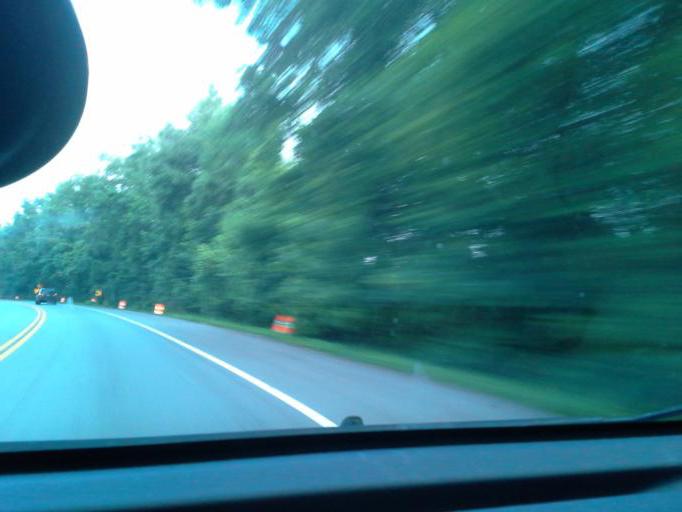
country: US
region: Maryland
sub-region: Anne Arundel County
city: Davidsonville
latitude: 38.8623
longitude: -76.6193
